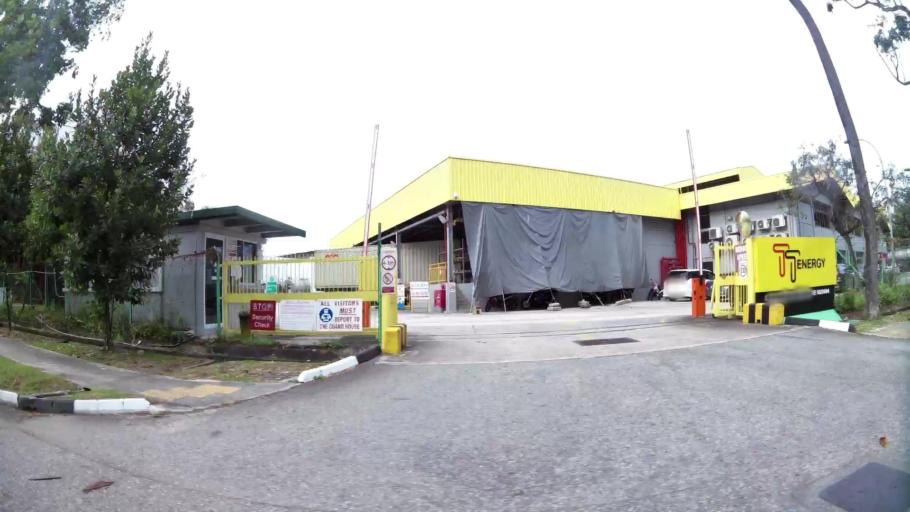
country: MY
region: Johor
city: Johor Bahru
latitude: 1.3109
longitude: 103.6648
